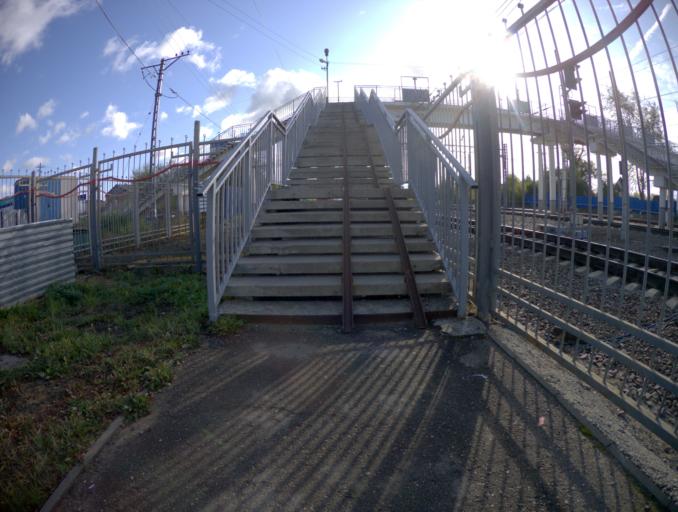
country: RU
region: Vladimir
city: Petushki
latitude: 55.9248
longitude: 39.4639
